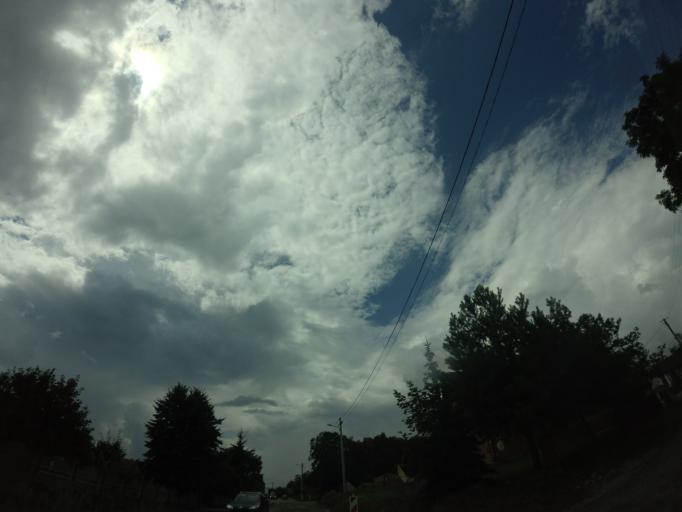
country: PL
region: Swietokrzyskie
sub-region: Powiat opatowski
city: Tarlow
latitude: 51.0342
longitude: 21.6827
